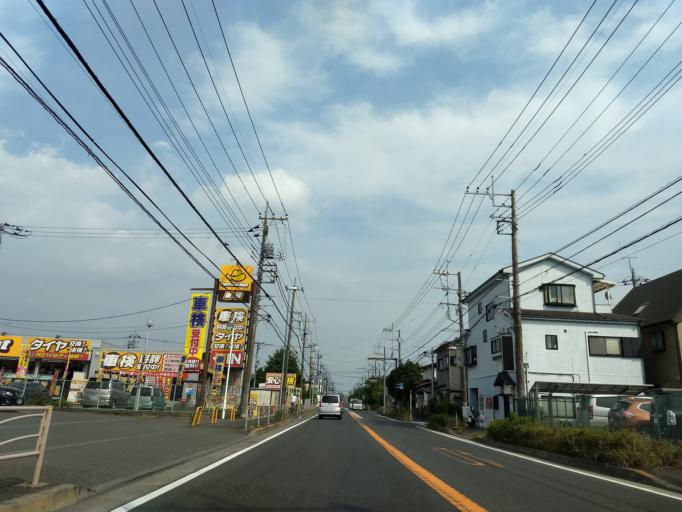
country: JP
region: Kanagawa
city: Minami-rinkan
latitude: 35.4926
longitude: 139.5117
